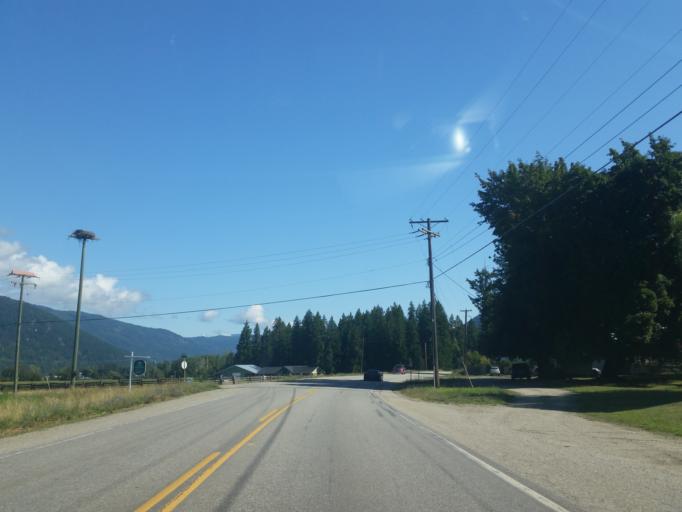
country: CA
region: British Columbia
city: Enderby
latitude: 50.6804
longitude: -119.0539
